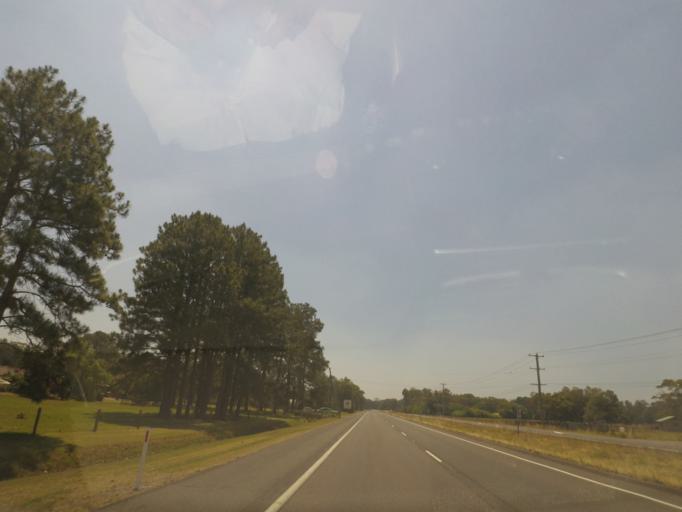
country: AU
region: New South Wales
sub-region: Port Stephens Shire
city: Medowie
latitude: -32.7925
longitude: 151.8978
